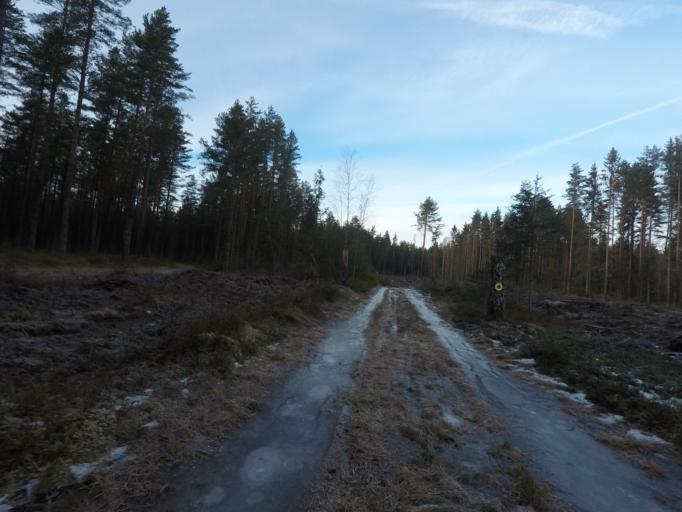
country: SE
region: Vaestmanland
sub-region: Kungsors Kommun
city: Kungsoer
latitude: 59.3442
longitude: 16.1183
